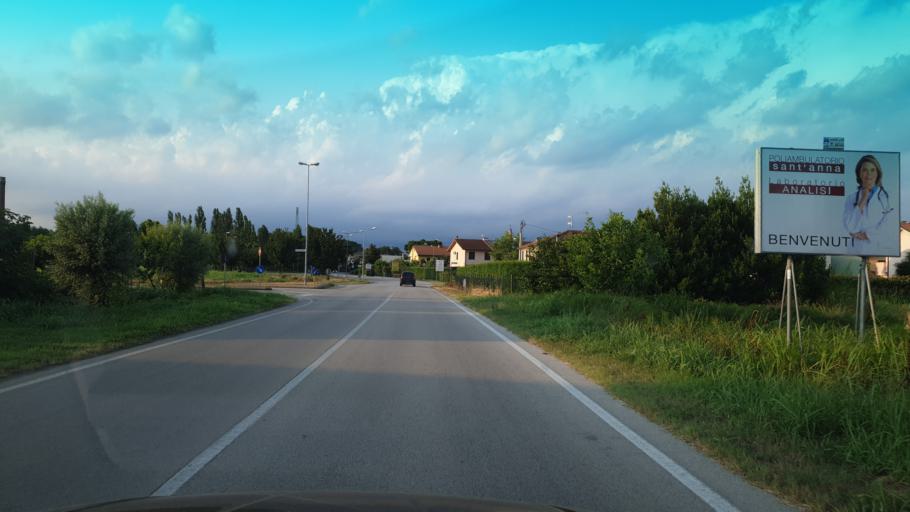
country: IT
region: Veneto
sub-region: Provincia di Rovigo
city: Lendinara
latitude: 45.0743
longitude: 11.5956
